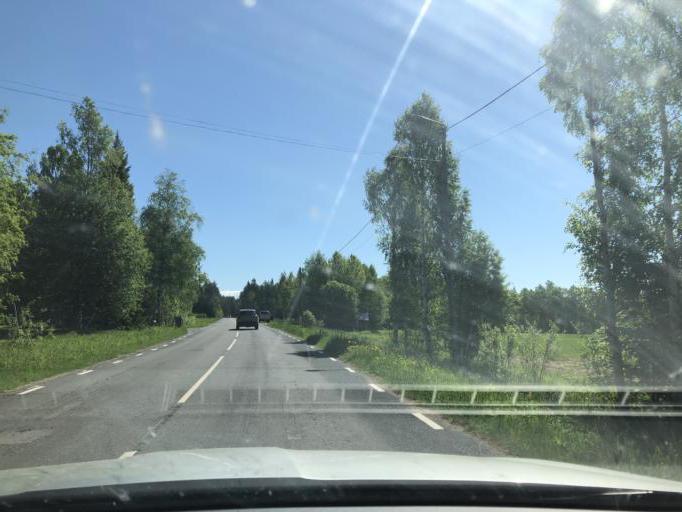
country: SE
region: Norrbotten
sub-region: Lulea Kommun
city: Gammelstad
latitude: 65.6570
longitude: 21.9999
